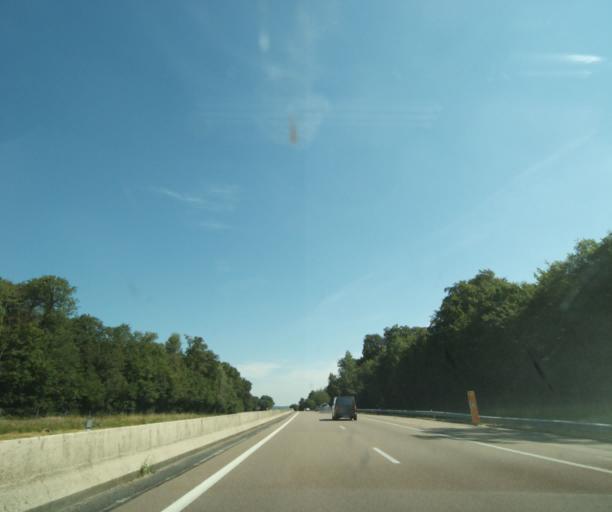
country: FR
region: Lorraine
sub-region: Departement de Meurthe-et-Moselle
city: Colombey-les-Belles
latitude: 48.4429
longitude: 5.8658
